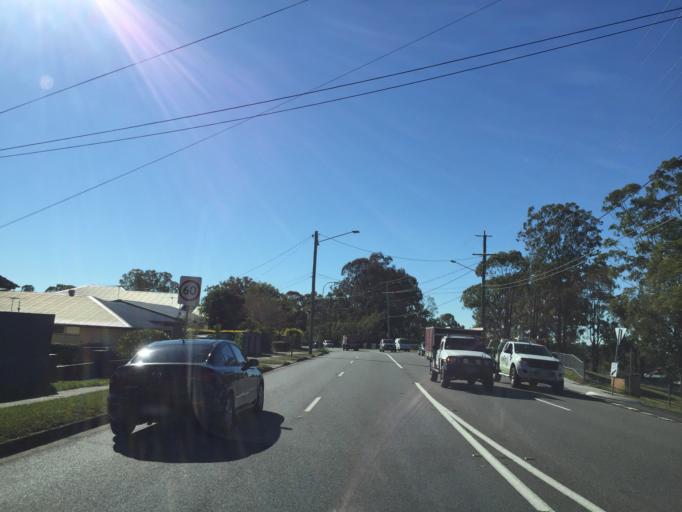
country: AU
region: Queensland
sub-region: Brisbane
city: Everton Park
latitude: -27.4116
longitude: 152.9640
